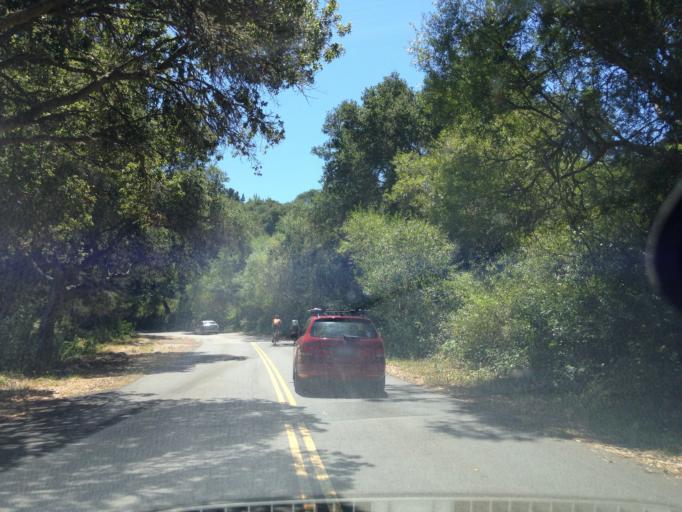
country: US
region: California
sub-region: Contra Costa County
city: Kensington
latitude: 37.9043
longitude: -122.2617
